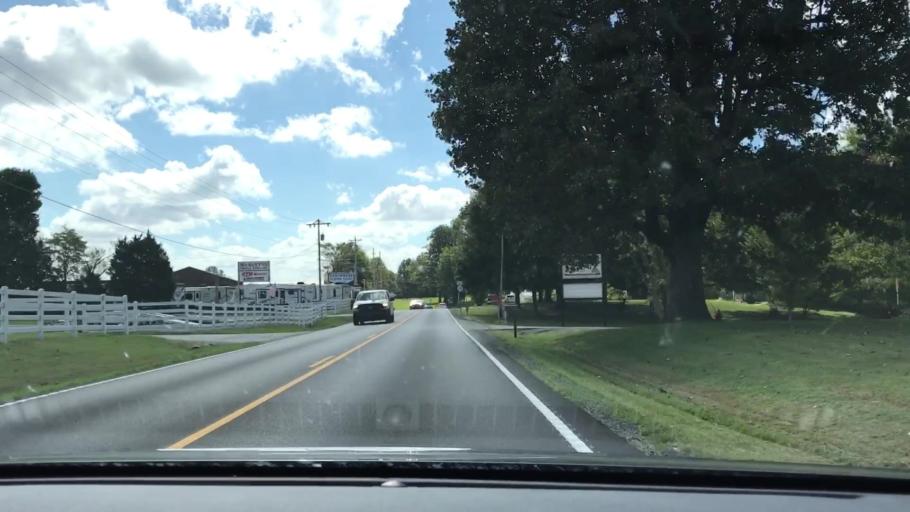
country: US
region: Kentucky
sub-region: Graves County
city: Mayfield
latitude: 36.7614
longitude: -88.5962
